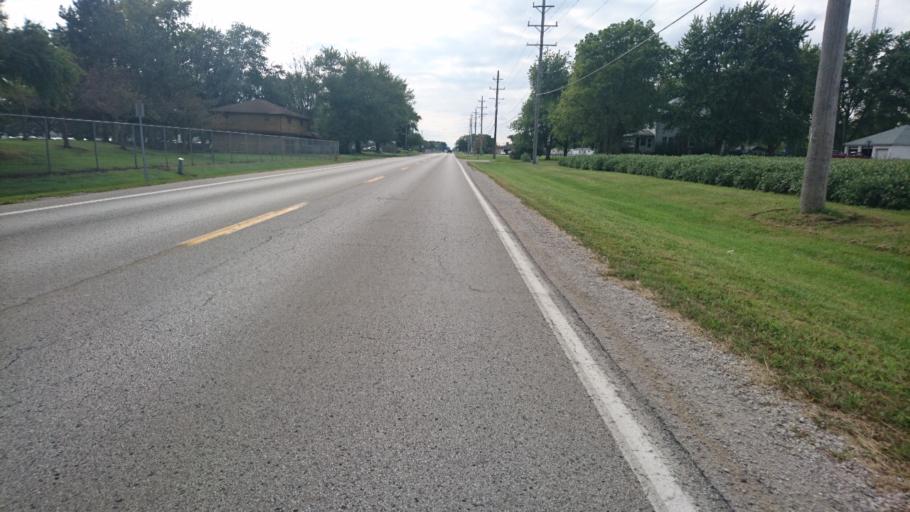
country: US
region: Illinois
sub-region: Livingston County
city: Pontiac
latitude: 40.8883
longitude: -88.6469
